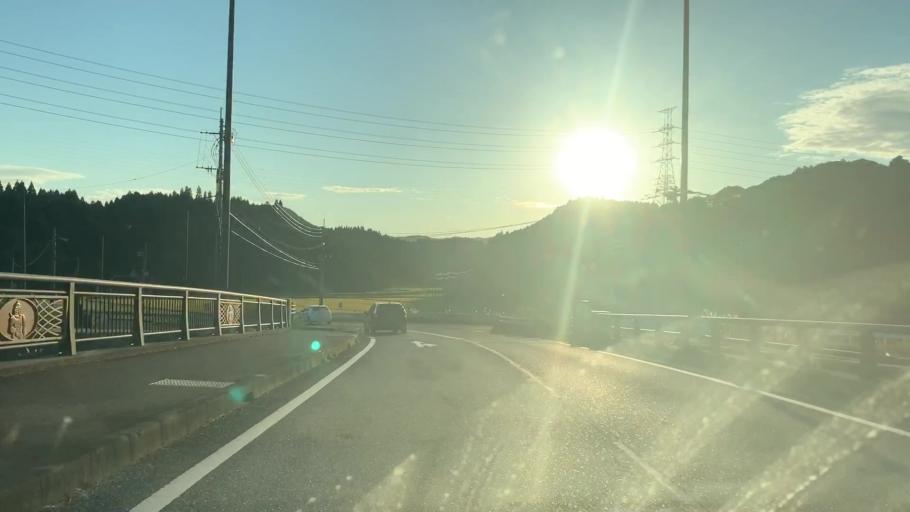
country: JP
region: Saga Prefecture
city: Karatsu
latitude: 33.3480
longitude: 129.9921
